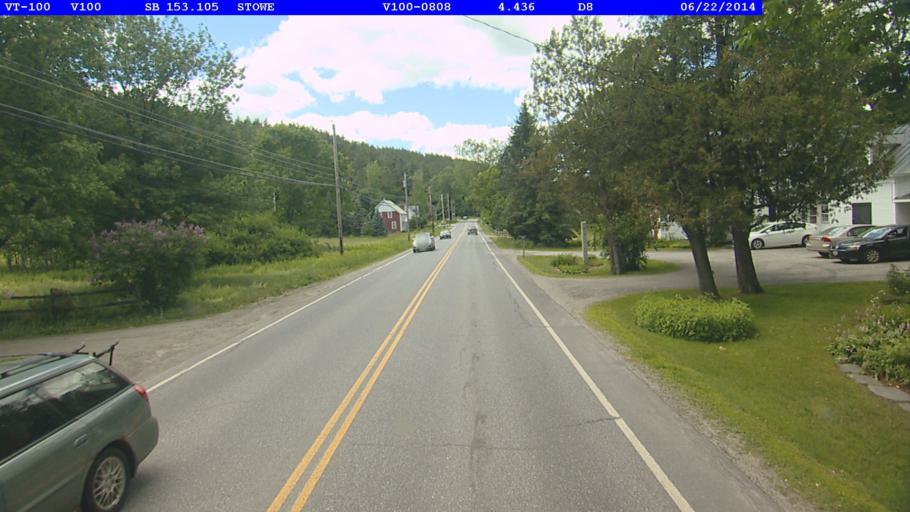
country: US
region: Vermont
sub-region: Lamoille County
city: Morristown
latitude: 44.4743
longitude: -72.6699
